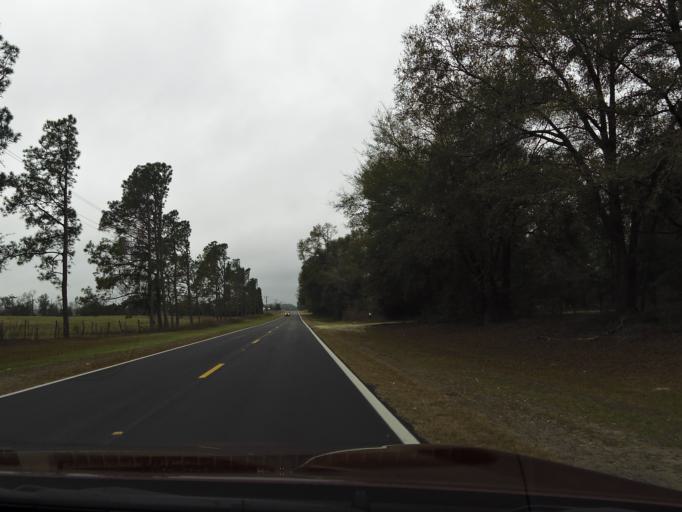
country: US
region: Florida
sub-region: Gilchrist County
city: Trenton
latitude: 29.7958
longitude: -82.8935
